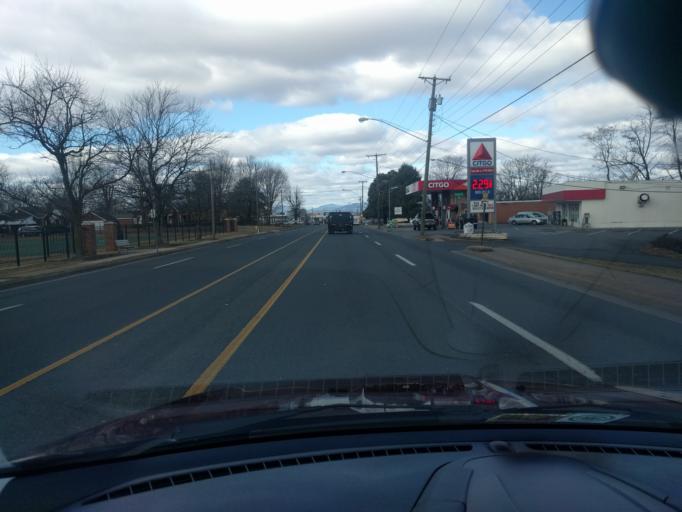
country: US
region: Virginia
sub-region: City of Lynchburg
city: Lynchburg
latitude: 37.3822
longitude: -79.1383
